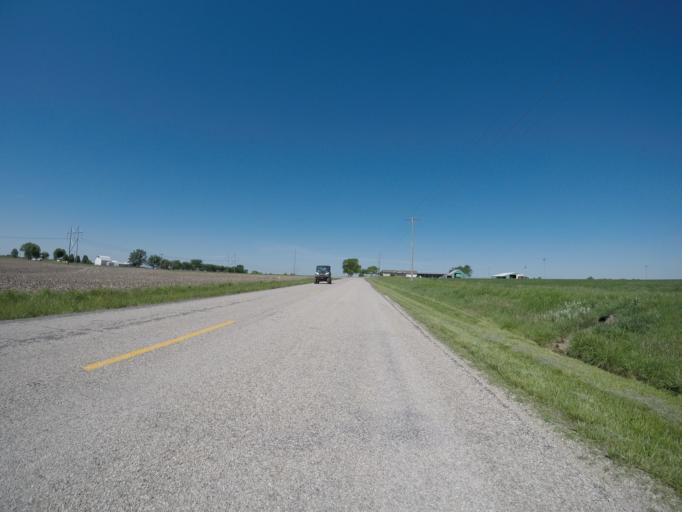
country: US
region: Kansas
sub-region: Osage County
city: Overbrook
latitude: 38.8405
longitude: -95.5545
